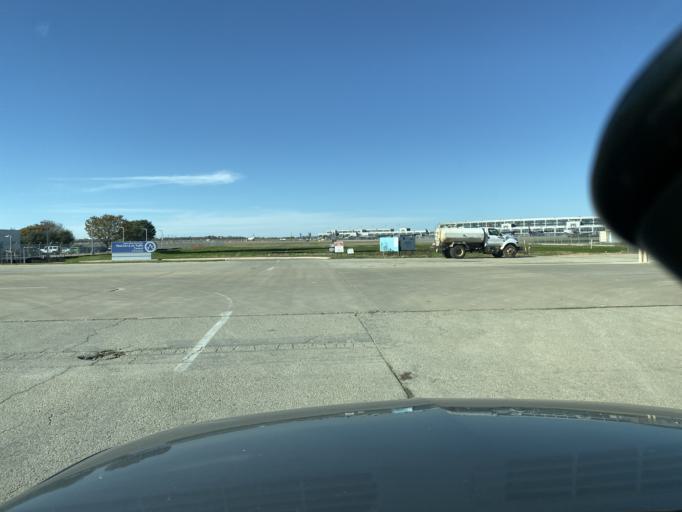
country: US
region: Texas
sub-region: Travis County
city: Hornsby Bend
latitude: 30.1962
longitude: -97.6644
